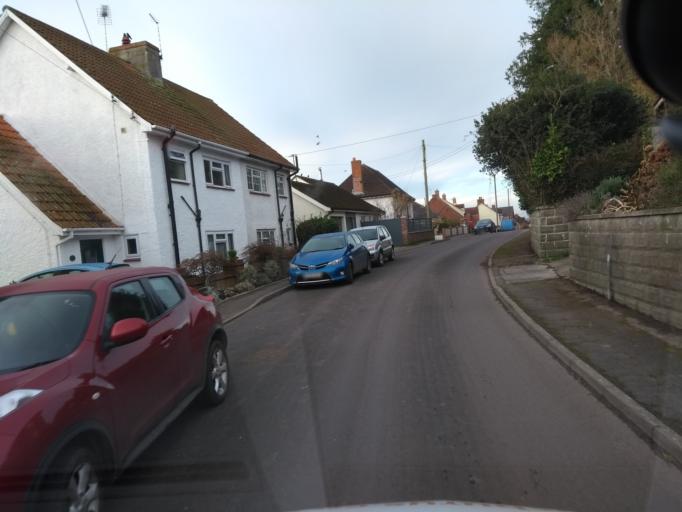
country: GB
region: England
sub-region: Somerset
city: Glastonbury
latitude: 51.1393
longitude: -2.7265
